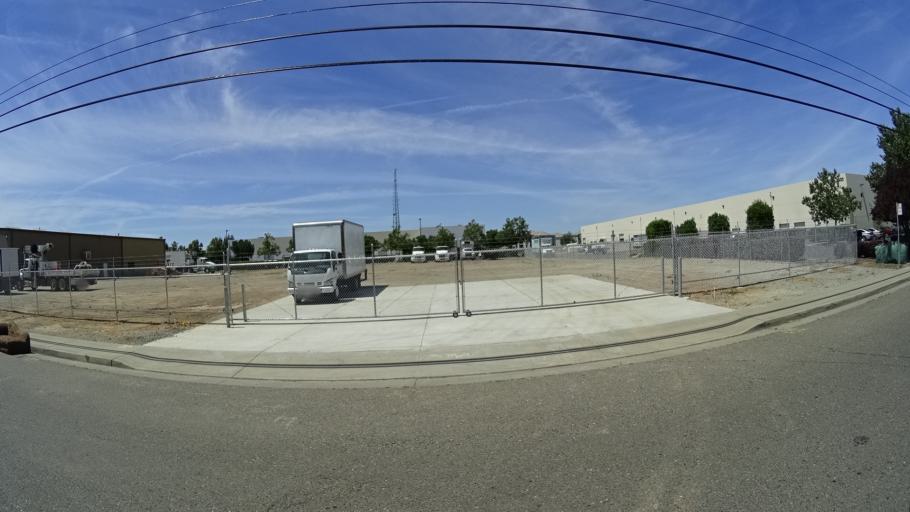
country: US
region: California
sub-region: Sacramento County
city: Rosemont
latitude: 38.5477
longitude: -121.4167
